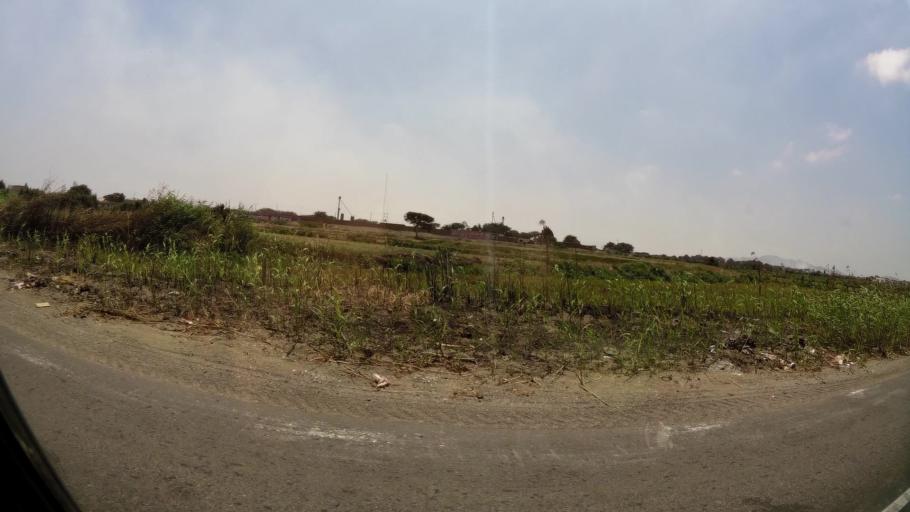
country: PE
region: La Libertad
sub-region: Provincia de Pacasmayo
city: Pacasmayo
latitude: -7.4197
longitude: -79.5429
